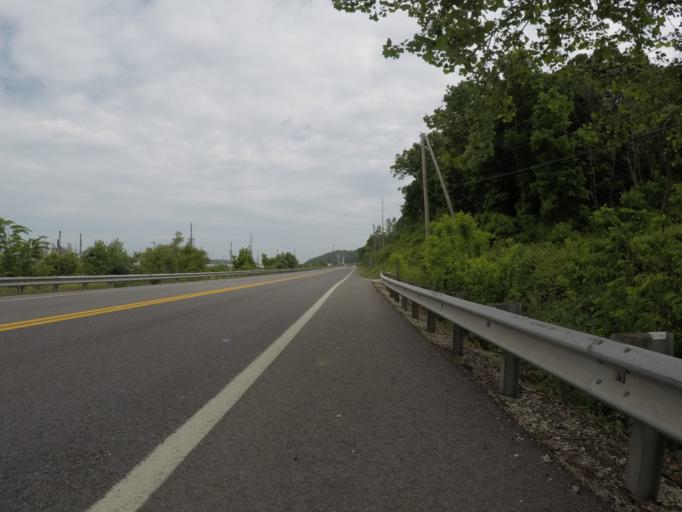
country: US
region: West Virginia
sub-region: Wayne County
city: Kenova
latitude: 38.3655
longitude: -82.5926
